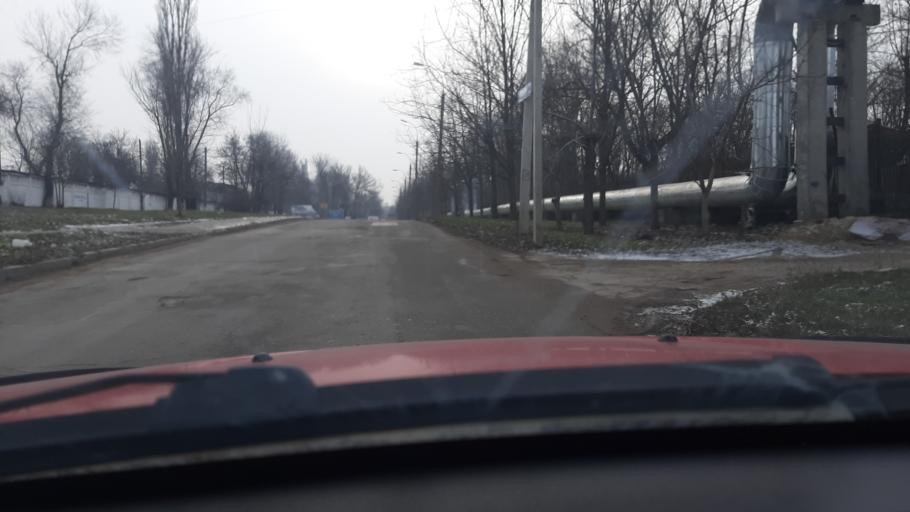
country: MD
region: Chisinau
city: Chisinau
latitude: 46.9772
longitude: 28.8922
